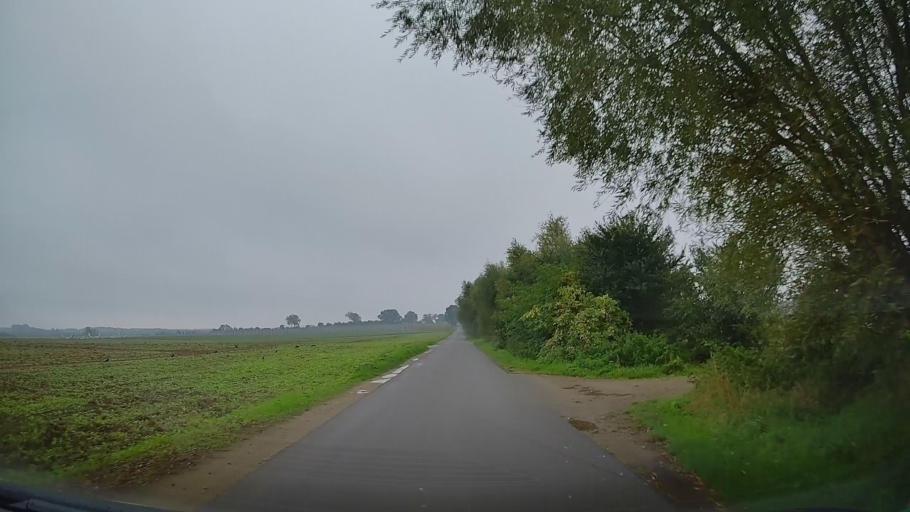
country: DE
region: Mecklenburg-Vorpommern
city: Gramkow
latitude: 53.9289
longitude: 11.3354
